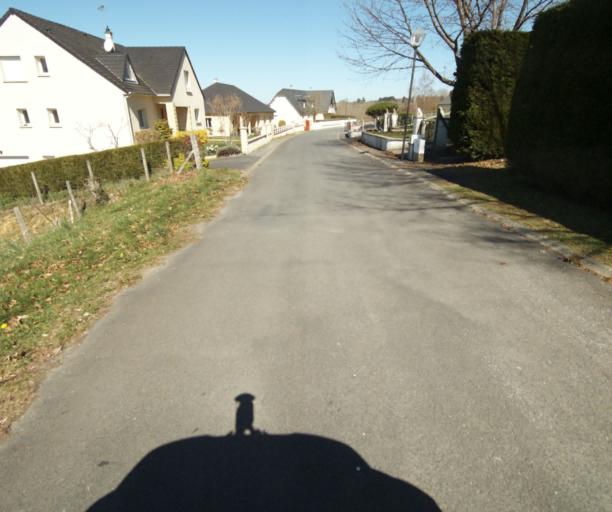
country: FR
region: Limousin
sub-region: Departement de la Correze
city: Seilhac
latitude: 45.3693
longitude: 1.7147
